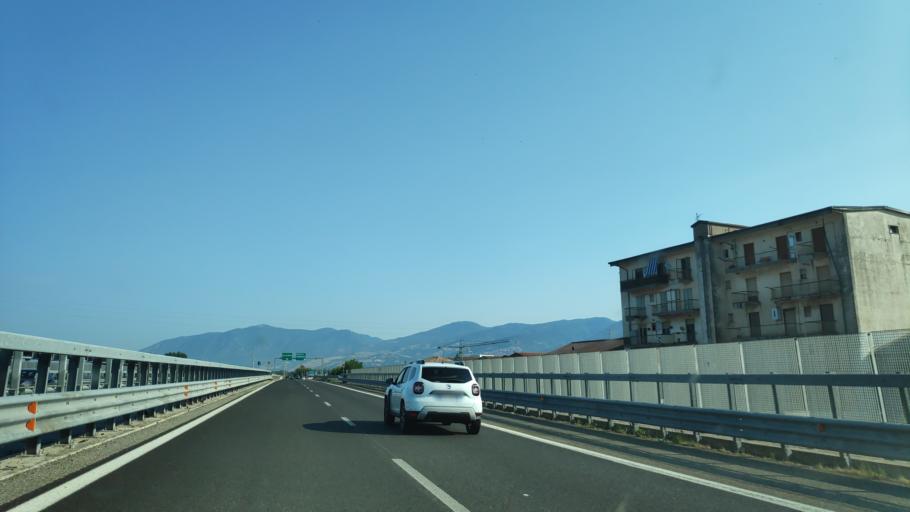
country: IT
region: Campania
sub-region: Provincia di Salerno
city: Buonabitacolo
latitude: 40.2943
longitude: 15.6484
